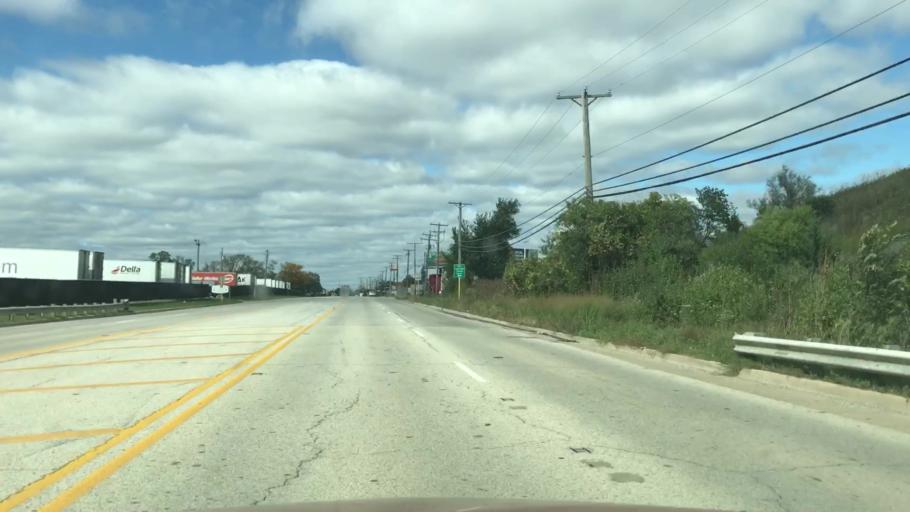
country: US
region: Illinois
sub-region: Cook County
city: Elk Grove Village
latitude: 42.0174
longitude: -87.9525
